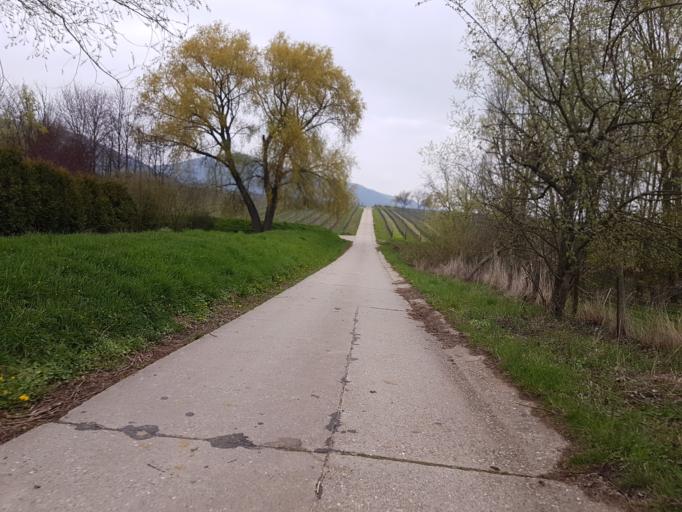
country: DE
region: Rheinland-Pfalz
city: Burrweiler
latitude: 49.2363
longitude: 8.0806
